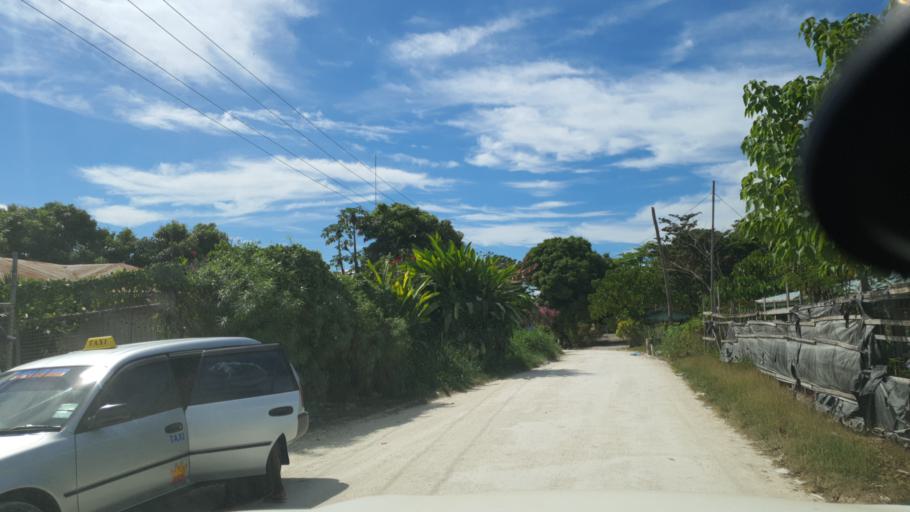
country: SB
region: Guadalcanal
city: Honiara
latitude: -9.4378
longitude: 159.9774
